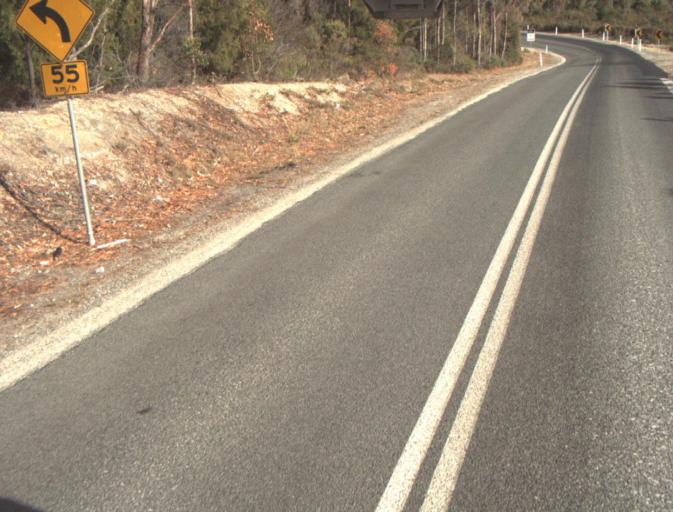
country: AU
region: Tasmania
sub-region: Dorset
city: Bridport
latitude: -41.1669
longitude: 147.2617
